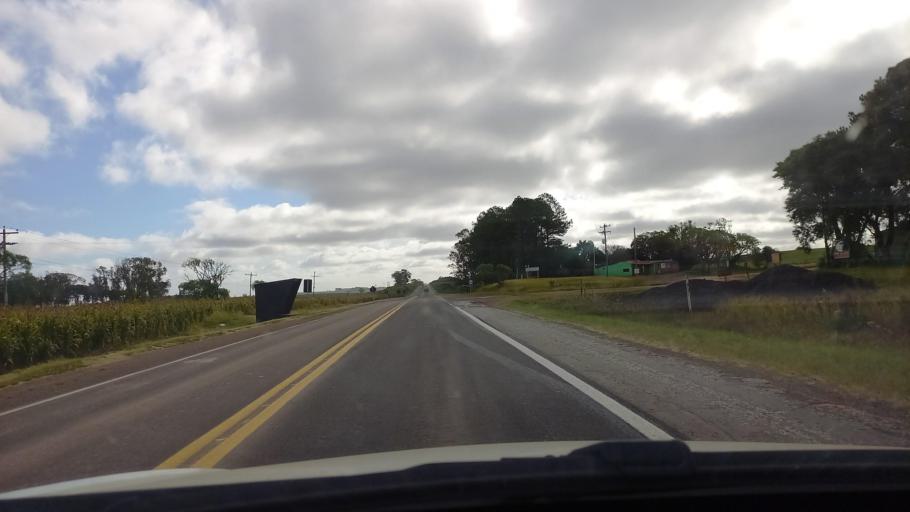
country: BR
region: Rio Grande do Sul
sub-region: Dom Pedrito
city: Dom Pedrito
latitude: -30.9025
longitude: -54.8309
